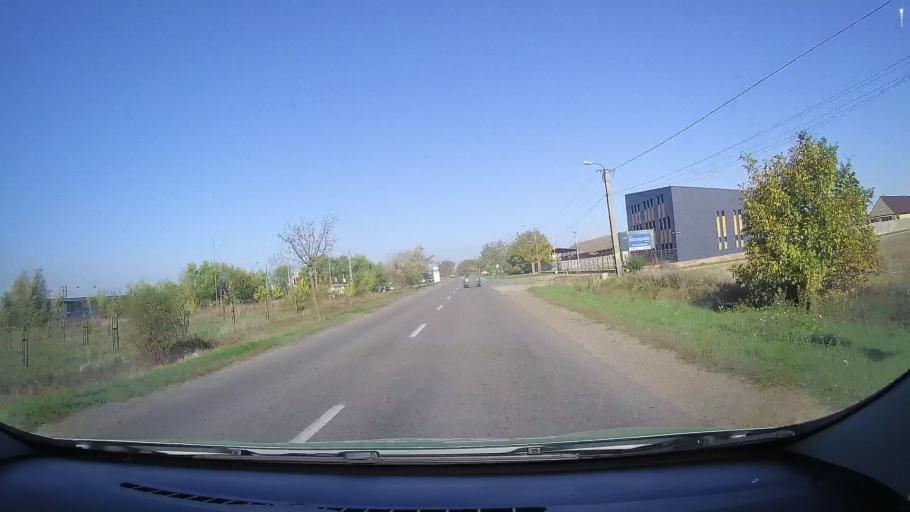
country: RO
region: Satu Mare
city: Carei
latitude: 47.6721
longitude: 22.4834
